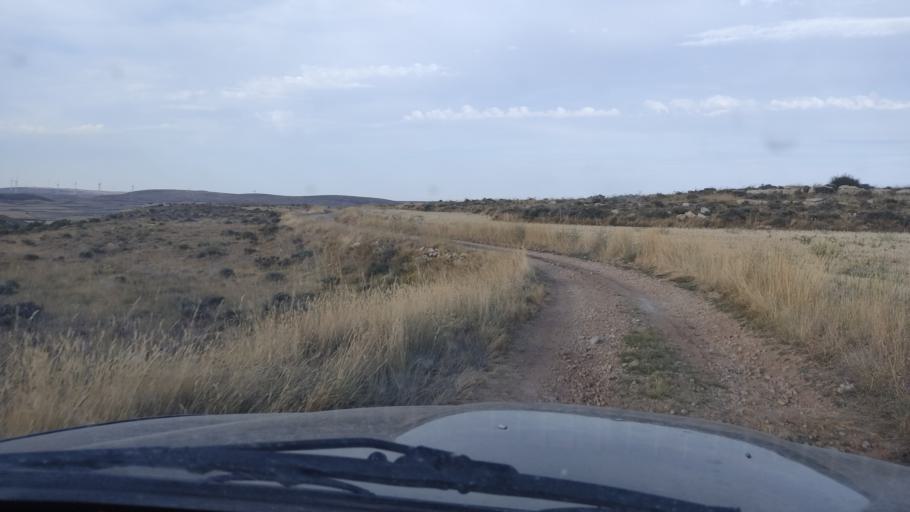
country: ES
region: Aragon
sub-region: Provincia de Teruel
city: Monforte de Moyuela
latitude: 41.0311
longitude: -0.9997
